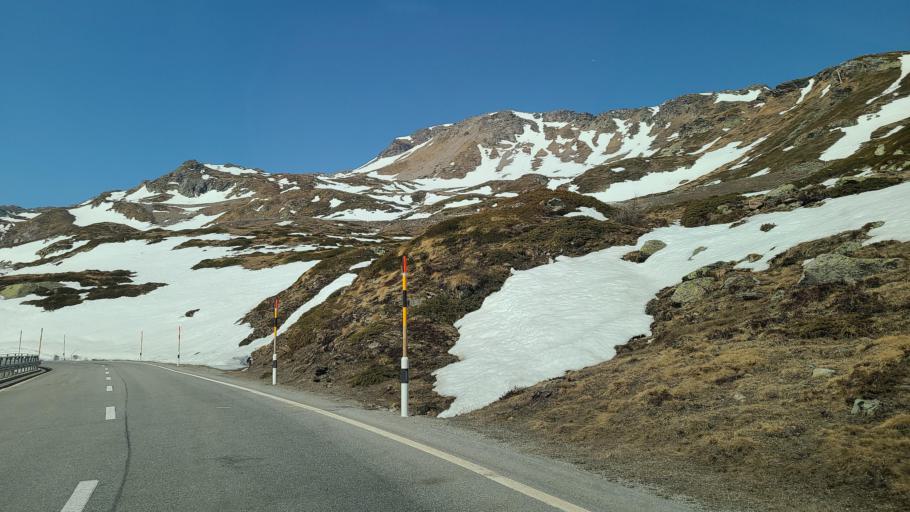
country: CH
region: Grisons
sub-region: Bernina District
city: Poschiavo
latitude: 46.4139
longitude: 10.0428
